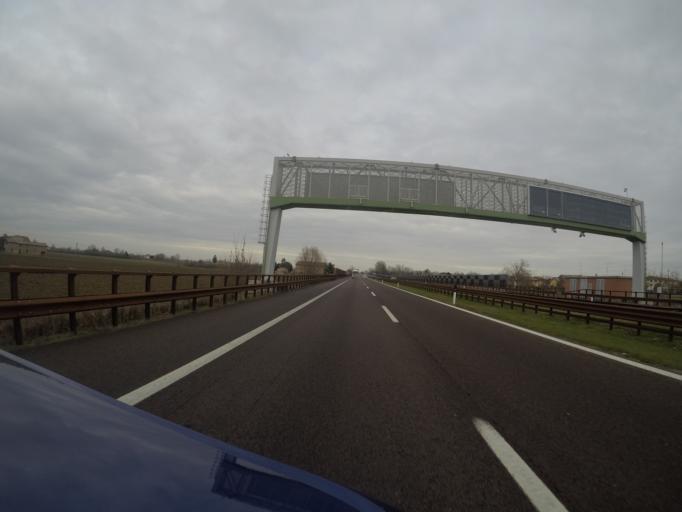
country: IT
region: Emilia-Romagna
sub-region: Provincia di Reggio Emilia
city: Rolo
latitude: 44.8810
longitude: 10.8500
